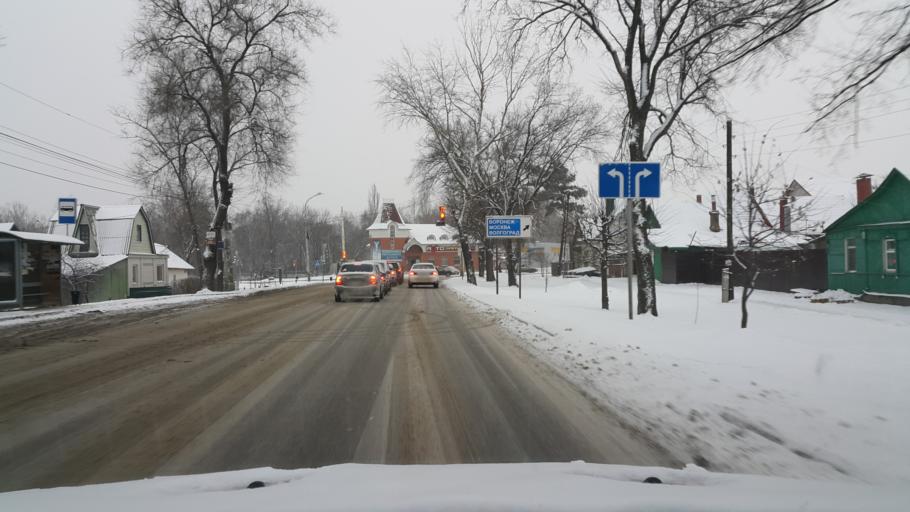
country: RU
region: Tambov
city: Pokrovo-Prigorodnoye
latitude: 52.7004
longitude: 41.4328
